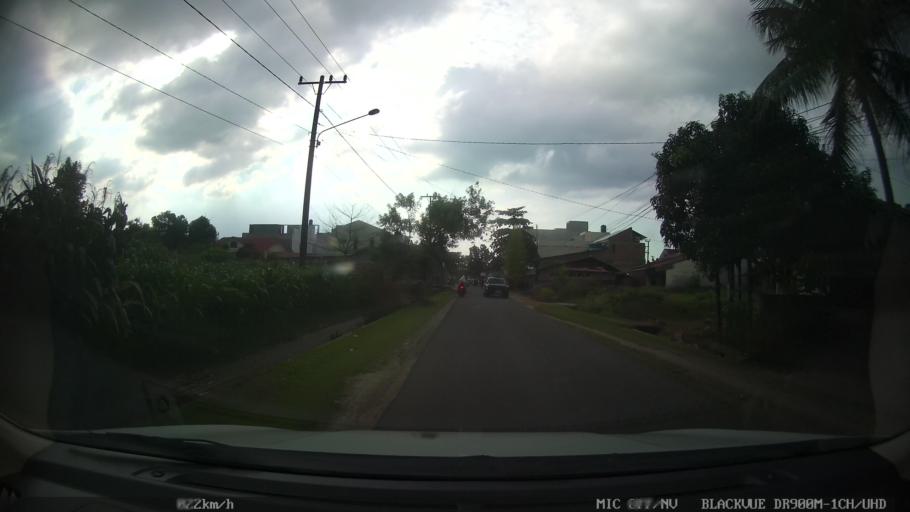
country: ID
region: North Sumatra
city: Sunggal
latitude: 3.5258
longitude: 98.6122
